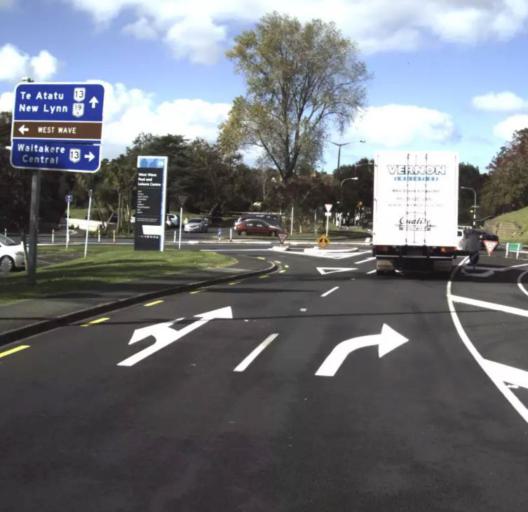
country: NZ
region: Auckland
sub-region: Auckland
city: Rosebank
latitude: -36.8766
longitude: 174.6331
